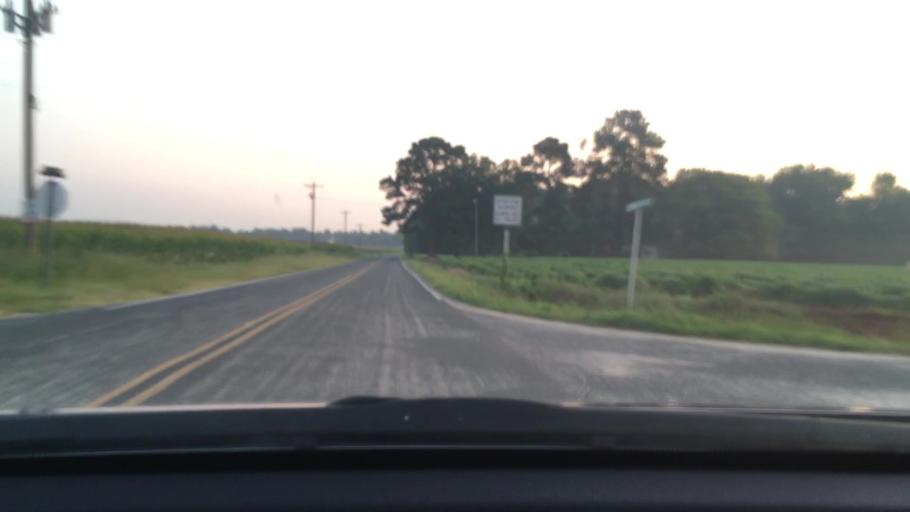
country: US
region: South Carolina
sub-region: Lee County
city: Bishopville
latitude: 34.1788
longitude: -80.1435
